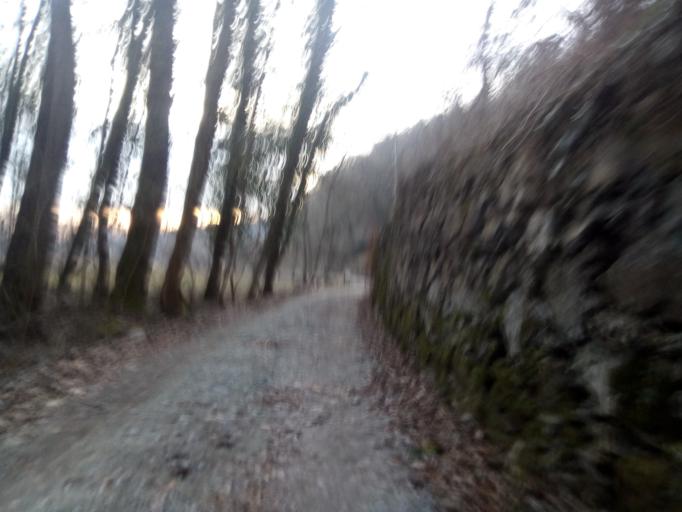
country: IT
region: Piedmont
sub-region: Provincia di Torino
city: Cascinette d'Ivrea
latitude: 45.4893
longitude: 7.9112
